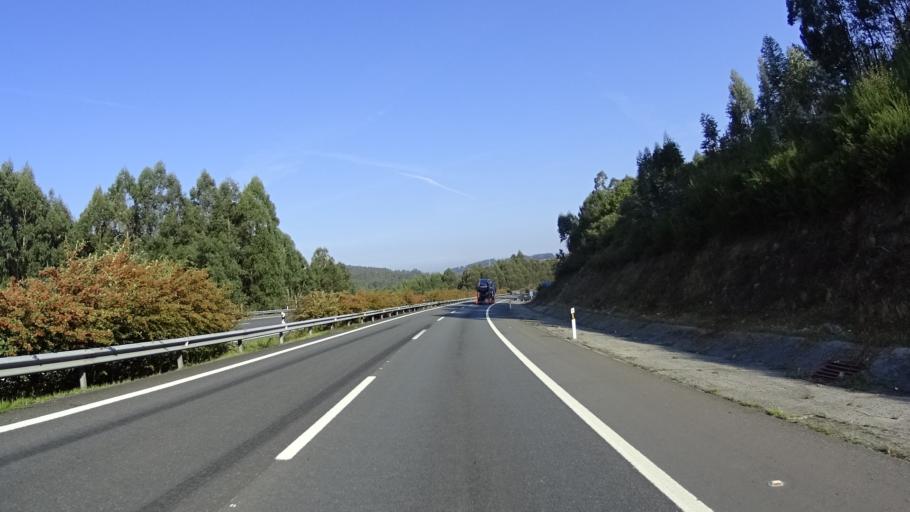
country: ES
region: Galicia
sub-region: Provincia da Coruna
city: Coiros
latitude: 43.2468
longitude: -8.1784
